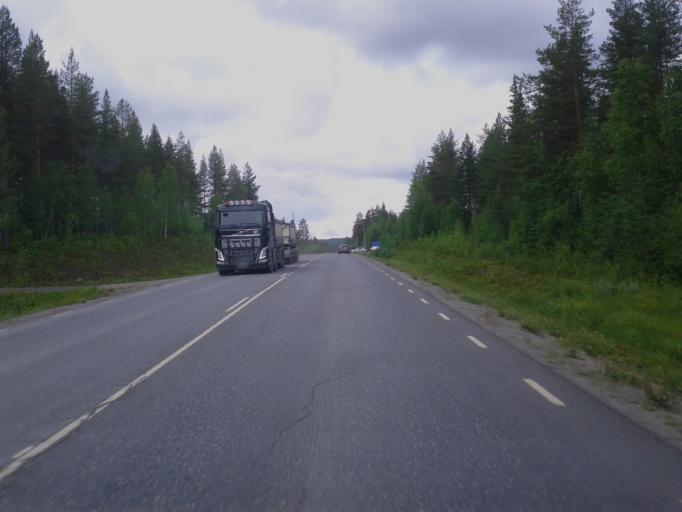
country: SE
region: Vaesterbotten
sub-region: Norsjo Kommun
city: Norsjoe
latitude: 64.9877
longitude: 19.4396
